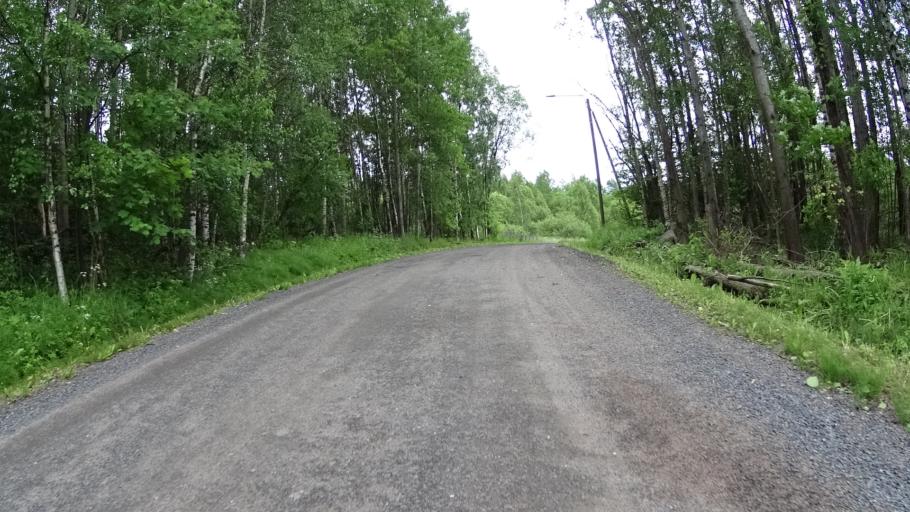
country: FI
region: Uusimaa
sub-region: Helsinki
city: Kilo
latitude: 60.2884
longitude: 24.8242
